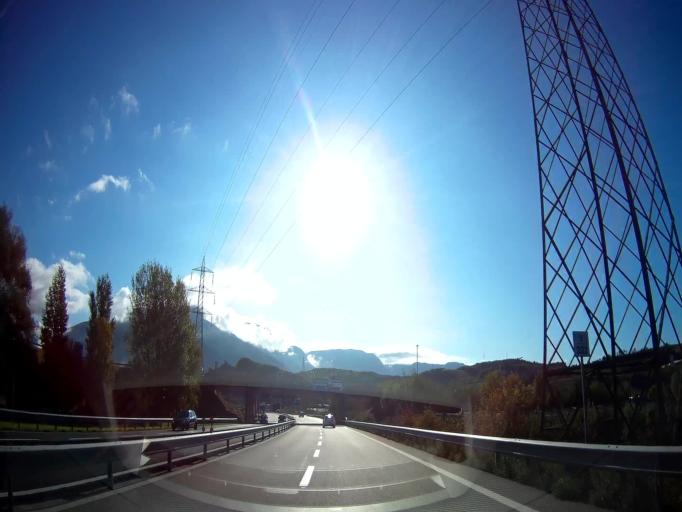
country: IT
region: Trentino-Alto Adige
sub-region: Bolzano
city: Cornaiano
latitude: 46.4868
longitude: 11.2889
